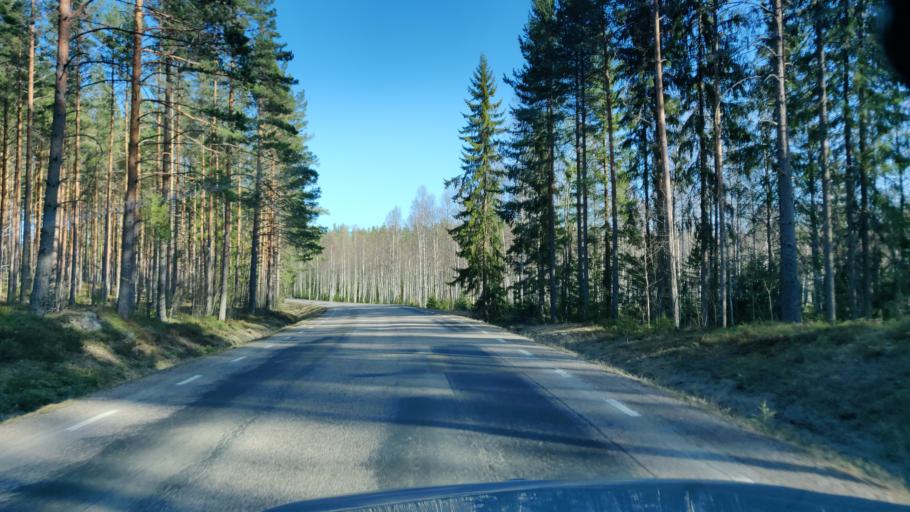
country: SE
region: Vaermland
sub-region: Sunne Kommun
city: Sunne
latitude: 59.9868
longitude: 13.3157
